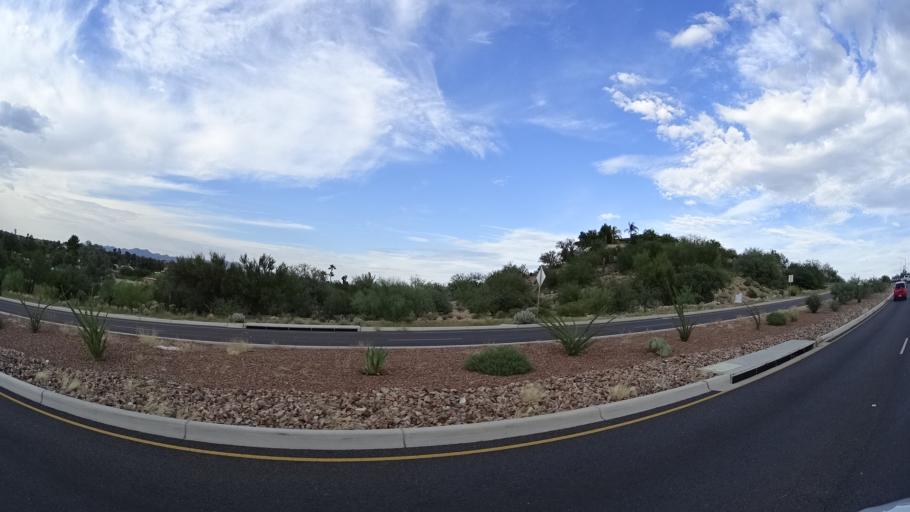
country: US
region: Arizona
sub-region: Pima County
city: Casas Adobes
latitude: 32.3472
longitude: -111.0229
